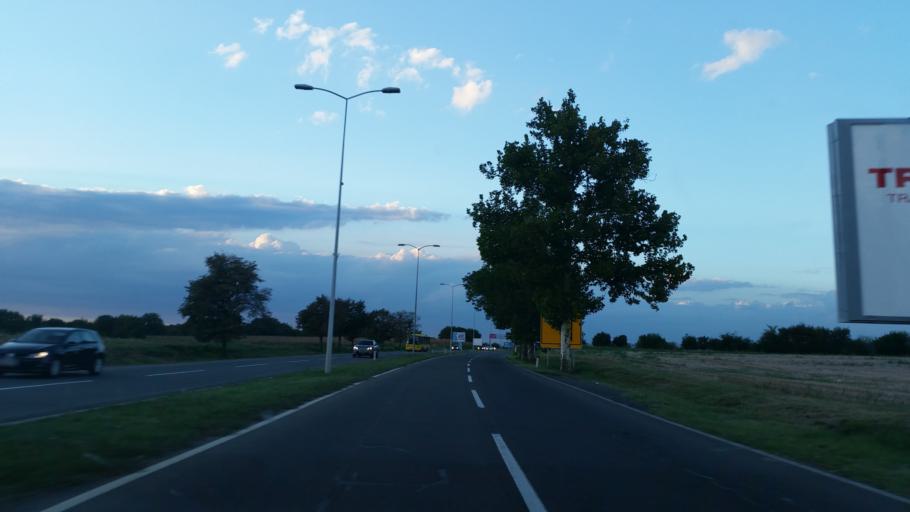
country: RS
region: Central Serbia
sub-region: Belgrade
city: Surcin
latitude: 44.8268
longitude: 20.2802
